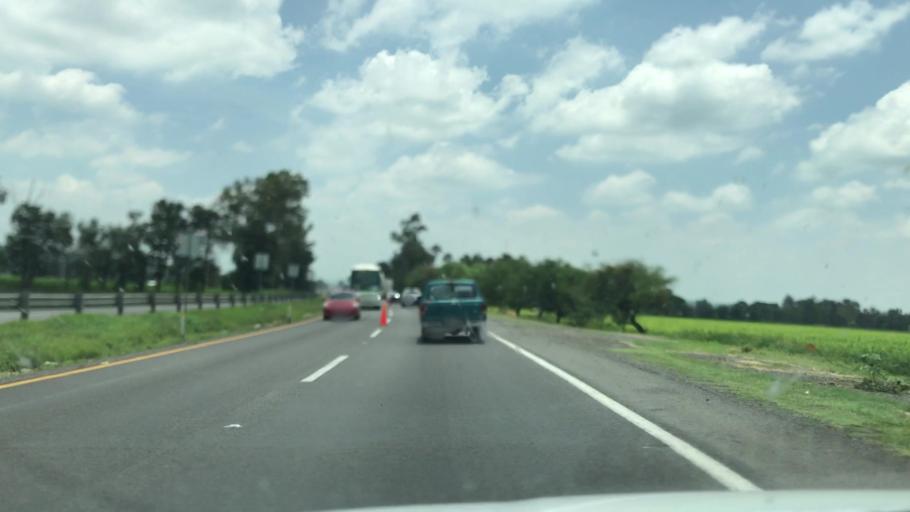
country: MX
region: Guanajuato
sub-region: Irapuato
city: San Ignacio de Rivera (Ojo de Agua)
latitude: 20.5180
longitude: -101.4649
